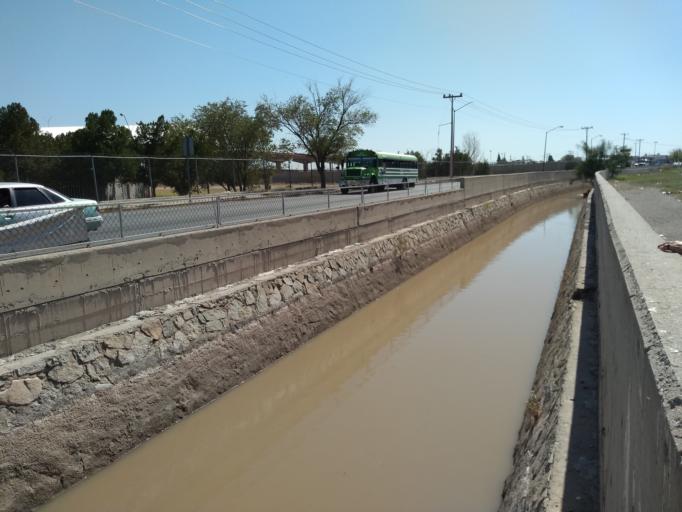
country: US
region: Texas
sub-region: El Paso County
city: El Paso
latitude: 31.7527
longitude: -106.4982
